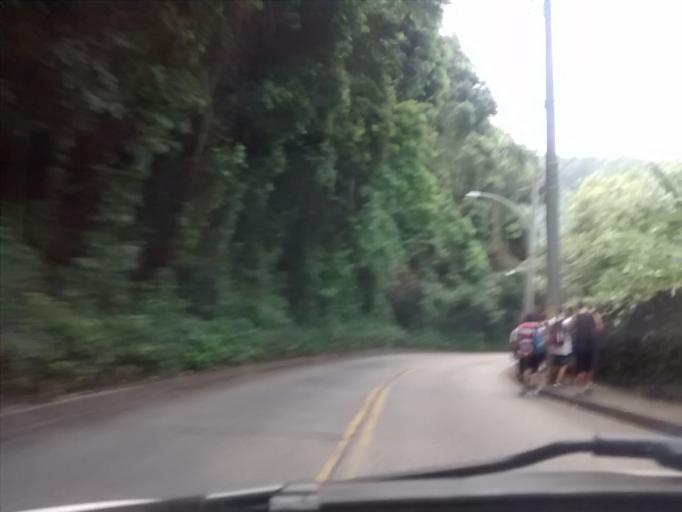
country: BR
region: Rio de Janeiro
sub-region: Rio De Janeiro
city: Rio de Janeiro
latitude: -22.9819
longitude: -43.2757
